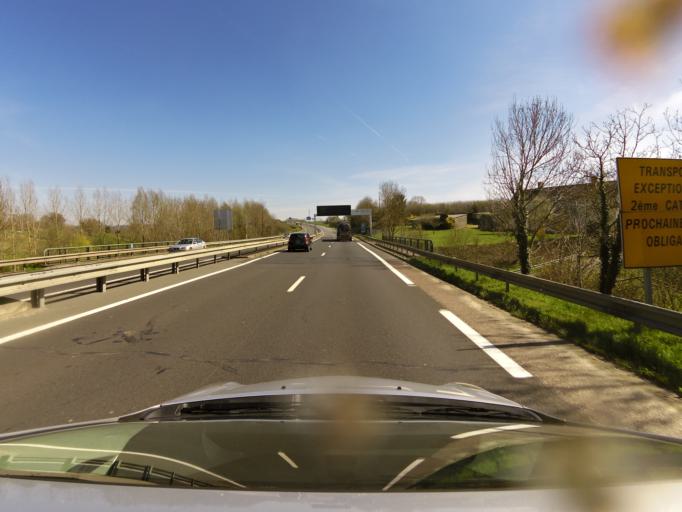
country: FR
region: Lower Normandy
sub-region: Departement de la Manche
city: Saint-Senier-sous-Avranches
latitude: 48.7029
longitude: -1.3414
